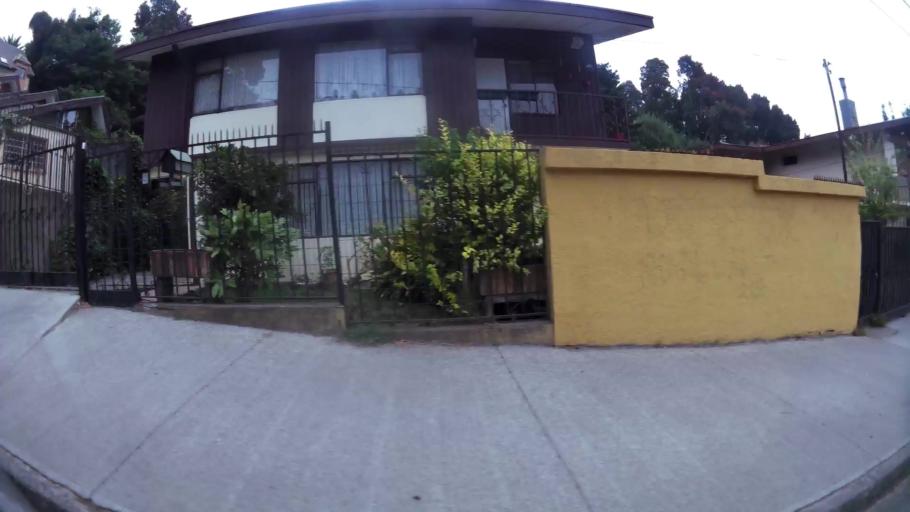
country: CL
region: Biobio
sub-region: Provincia de Concepcion
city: Concepcion
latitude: -36.8331
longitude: -73.0369
